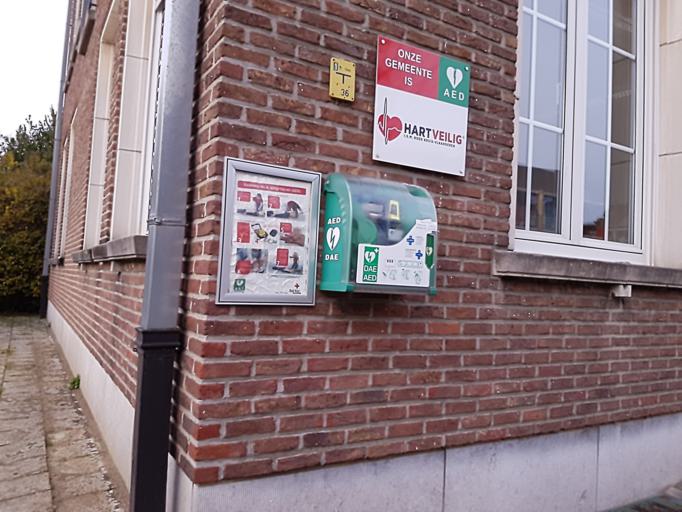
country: BE
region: Flanders
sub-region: Provincie Antwerpen
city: Putte
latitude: 51.0583
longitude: 4.6678
